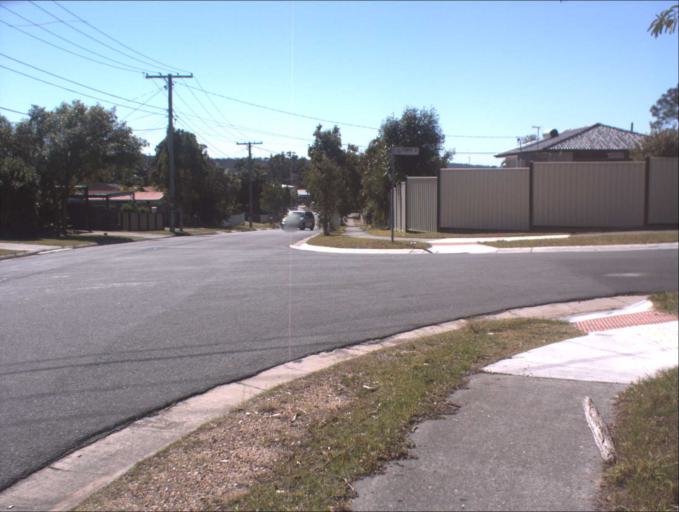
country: AU
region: Queensland
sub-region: Logan
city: Logan City
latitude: -27.6264
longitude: 153.1129
